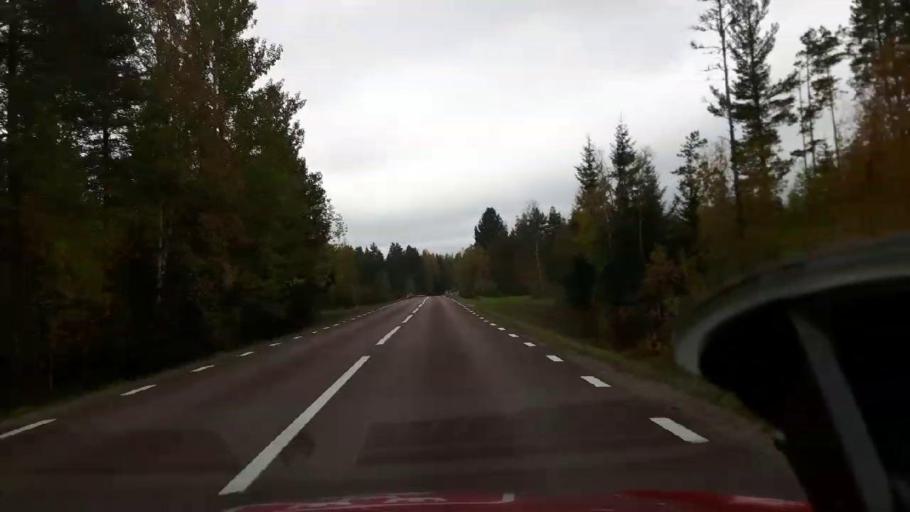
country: SE
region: Jaemtland
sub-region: Harjedalens Kommun
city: Sveg
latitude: 62.2211
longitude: 14.8490
